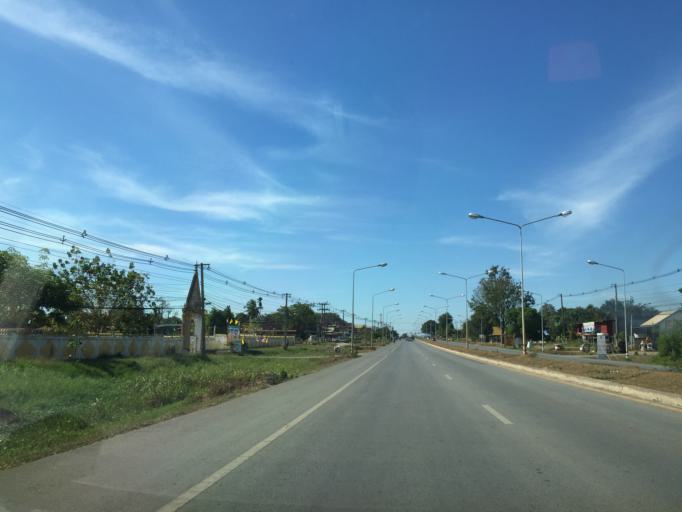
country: TH
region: Changwat Nong Bua Lamphu
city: Na Klang
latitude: 17.3073
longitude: 102.1846
